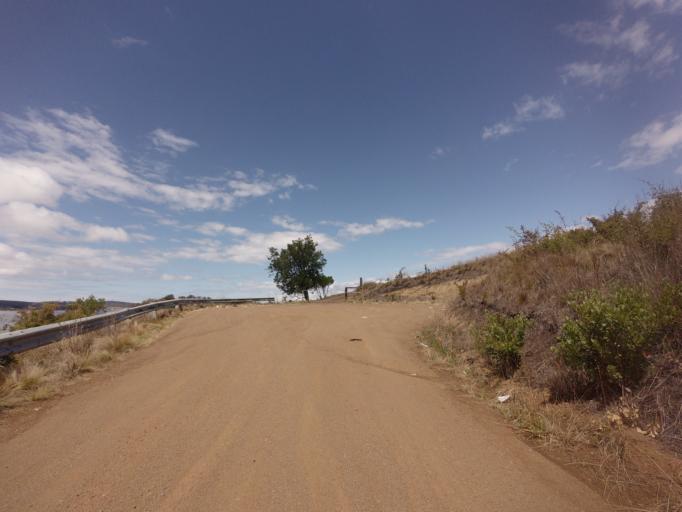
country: AU
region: Tasmania
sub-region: Clarence
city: Rokeby
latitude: -42.9201
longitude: 147.4336
